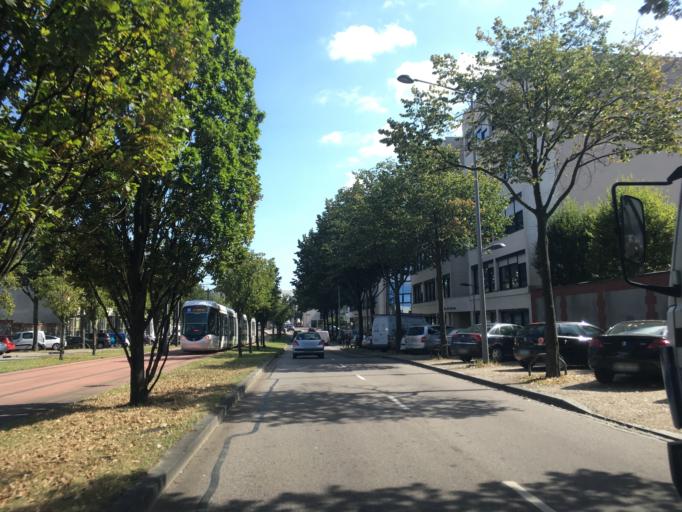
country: FR
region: Haute-Normandie
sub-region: Departement de la Seine-Maritime
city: Sotteville-les-Rouen
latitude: 49.4267
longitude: 1.0846
